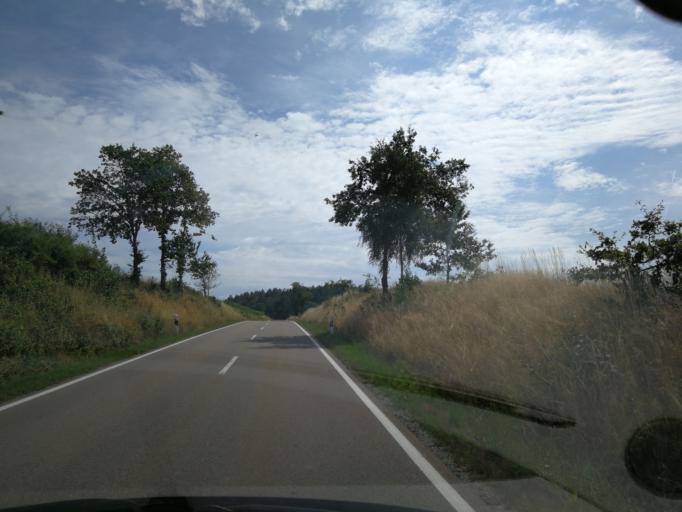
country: DE
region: Bavaria
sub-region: Lower Bavaria
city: Wiesenfelden
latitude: 49.0450
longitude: 12.5508
